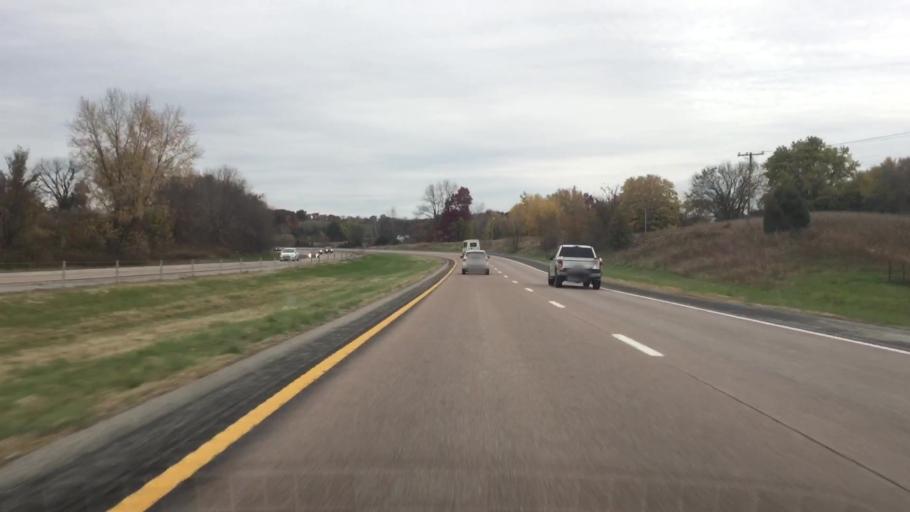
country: US
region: Missouri
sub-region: Cole County
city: Jefferson City
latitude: 38.6480
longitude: -92.2029
